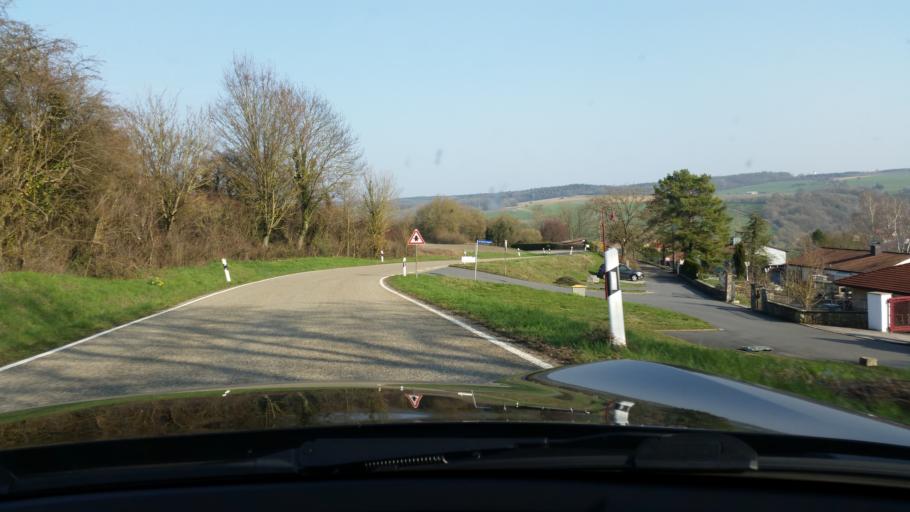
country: DE
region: Baden-Wuerttemberg
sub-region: Regierungsbezirk Stuttgart
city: Jagsthausen
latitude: 49.3191
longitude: 9.4663
